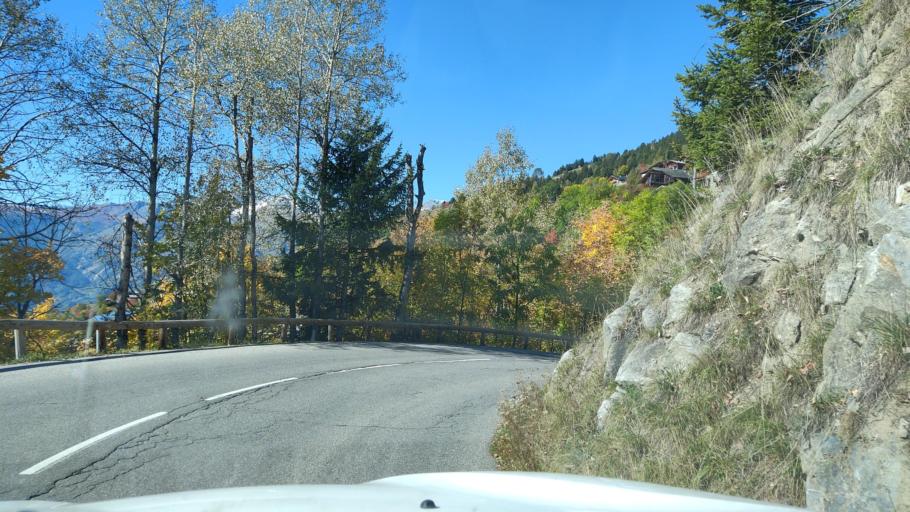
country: FR
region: Rhone-Alpes
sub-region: Departement de la Savoie
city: Seez
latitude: 45.6154
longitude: 6.8586
